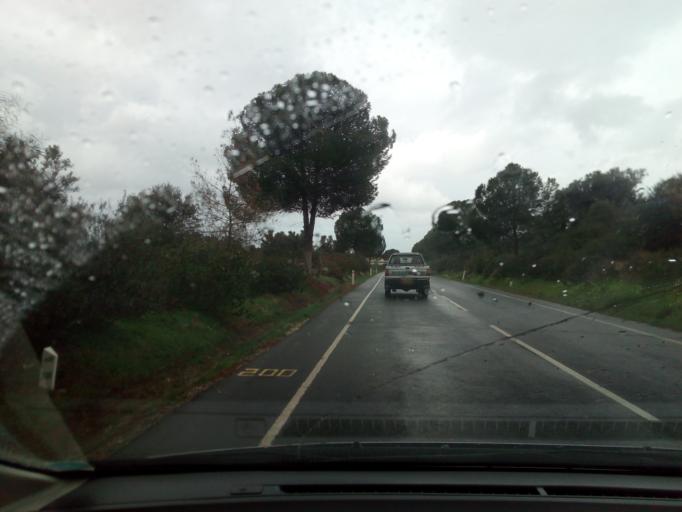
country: CY
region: Pafos
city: Polis
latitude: 35.0175
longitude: 32.4343
